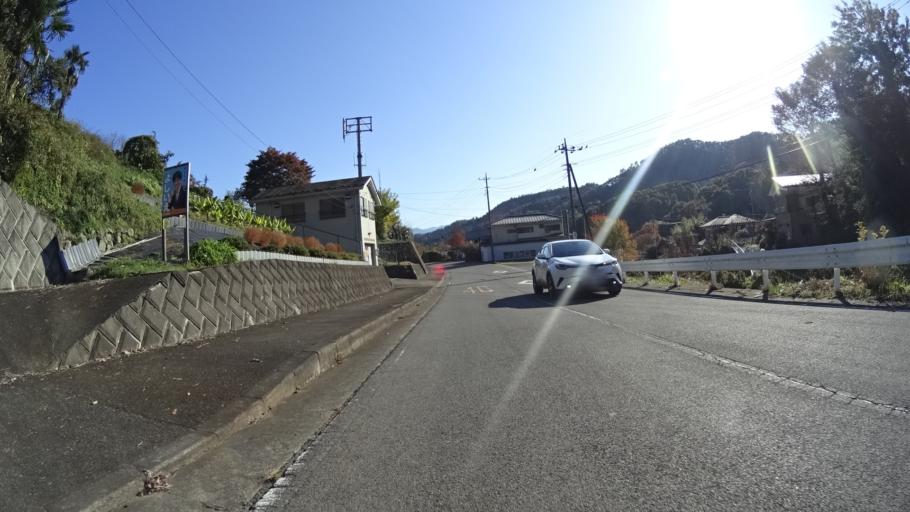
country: JP
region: Yamanashi
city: Uenohara
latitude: 35.6538
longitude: 139.1200
